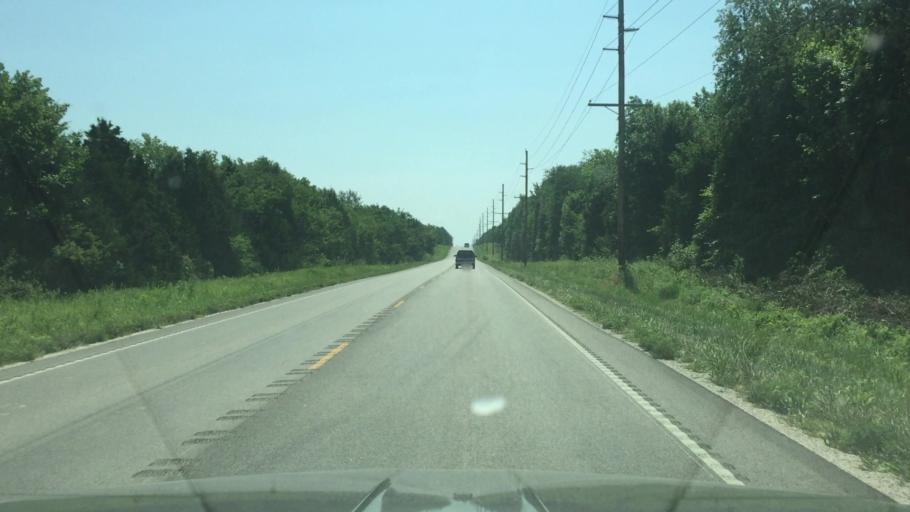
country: US
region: Missouri
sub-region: Morgan County
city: Versailles
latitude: 38.4002
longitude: -92.7399
